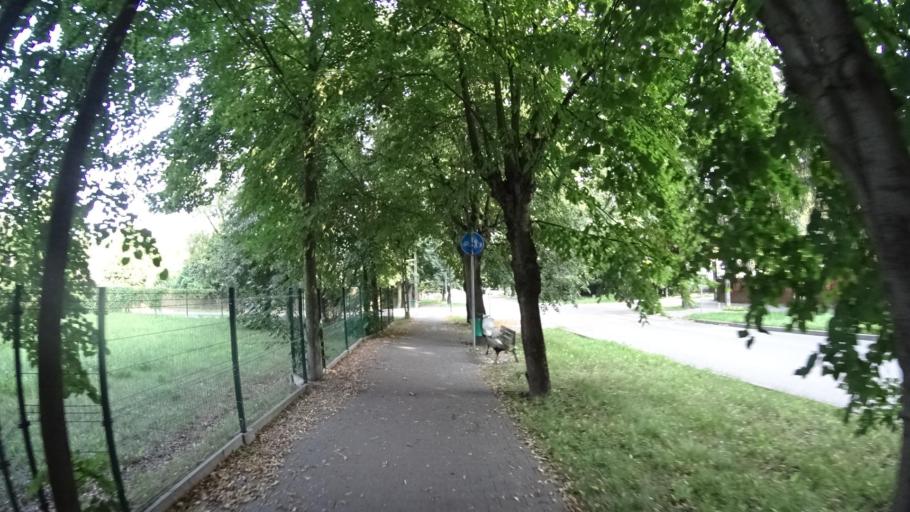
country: PL
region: Masovian Voivodeship
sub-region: Powiat pruszkowski
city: Michalowice
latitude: 52.1716
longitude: 20.8850
